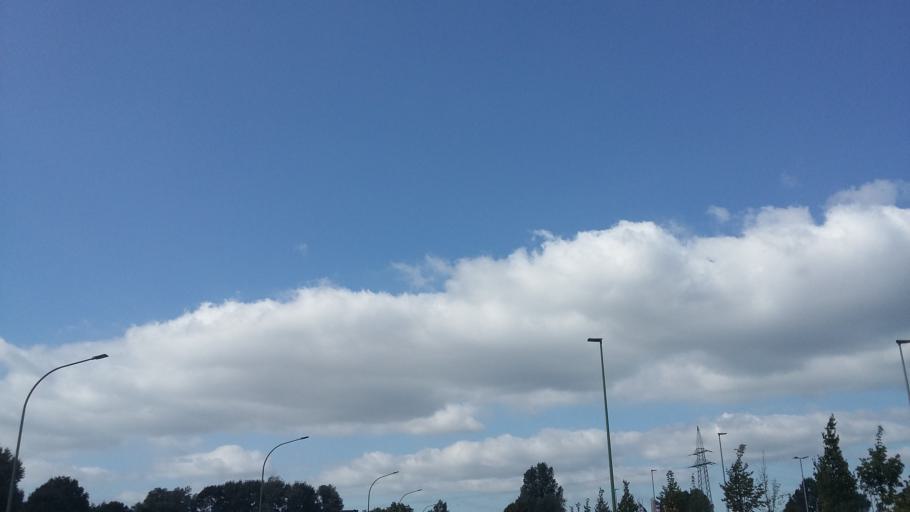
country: DE
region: Lower Saxony
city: Loxstedt
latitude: 53.4879
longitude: 8.6031
